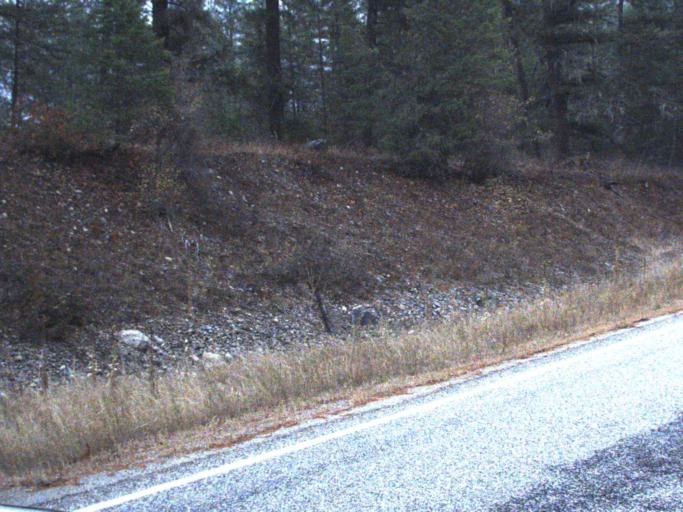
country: CA
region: British Columbia
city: Grand Forks
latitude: 48.9633
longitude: -118.2160
